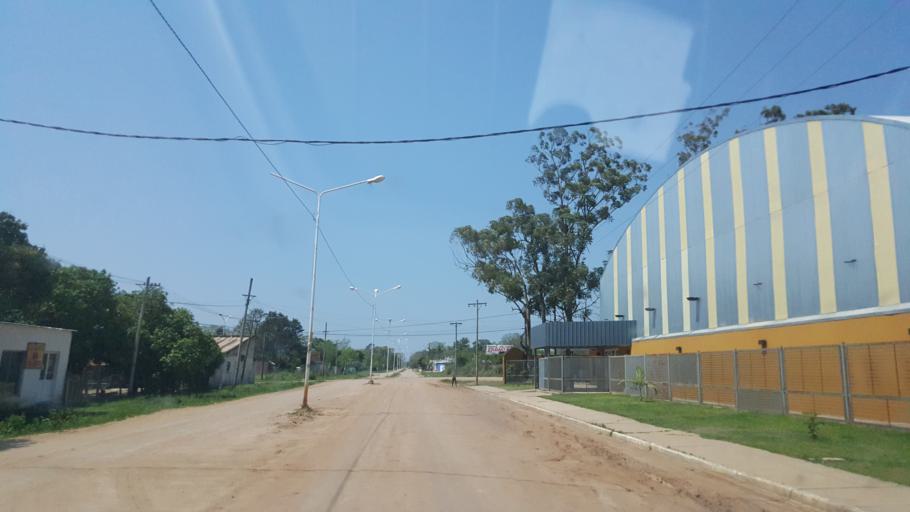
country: AR
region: Corrientes
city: Ita Ibate
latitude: -27.4285
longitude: -57.3432
